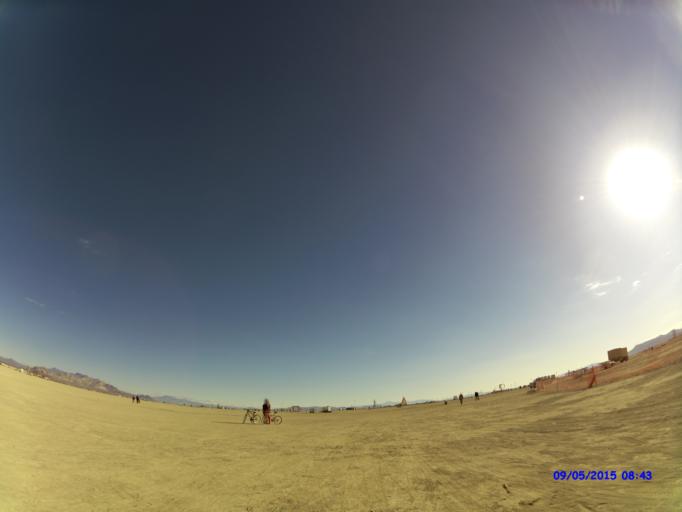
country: US
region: Nevada
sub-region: Pershing County
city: Lovelock
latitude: 40.7866
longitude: -119.2072
